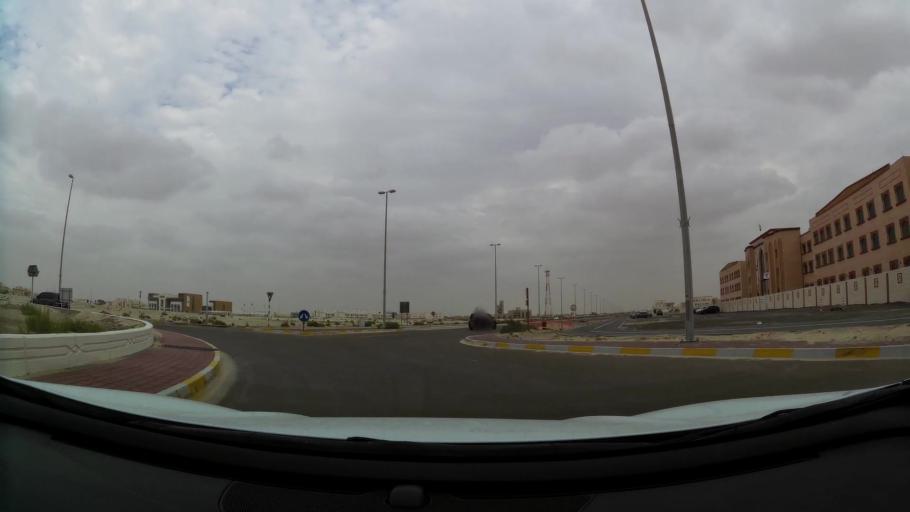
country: AE
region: Abu Dhabi
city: Abu Dhabi
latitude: 24.3622
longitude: 54.6329
